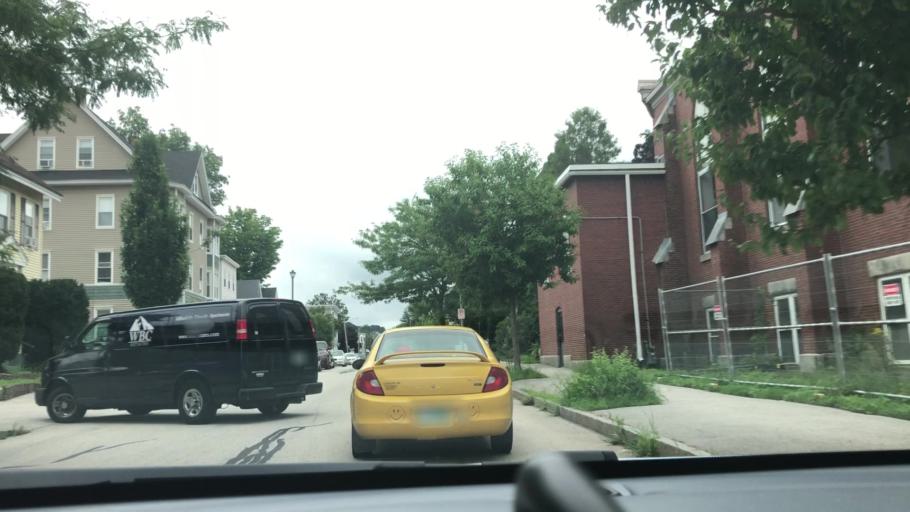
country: US
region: New Hampshire
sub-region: Hillsborough County
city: Manchester
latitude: 42.9893
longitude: -71.4571
